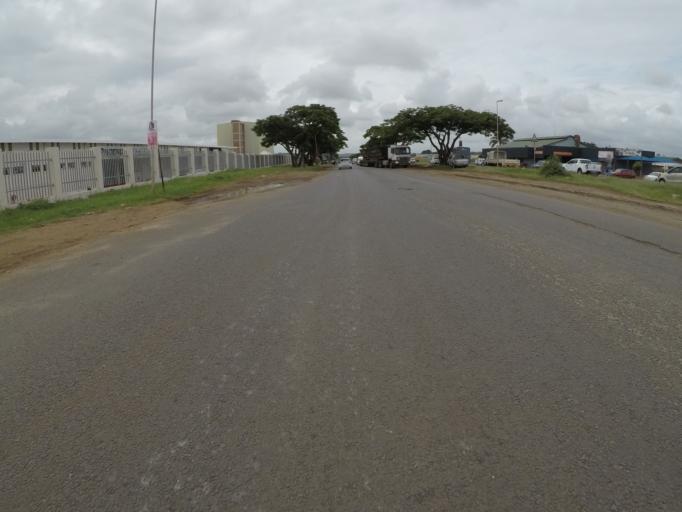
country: ZA
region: KwaZulu-Natal
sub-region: uThungulu District Municipality
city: Empangeni
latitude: -28.7778
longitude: 31.8997
